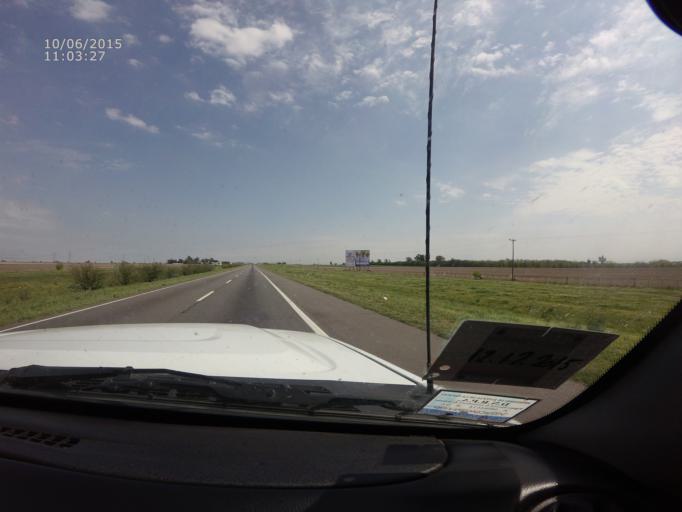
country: AR
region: Santa Fe
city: Arroyo Seco
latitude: -33.2363
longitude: -60.4470
